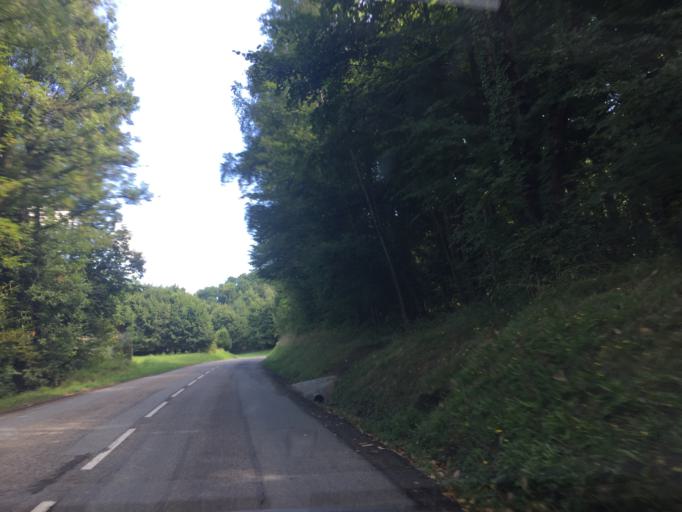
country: FR
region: Rhone-Alpes
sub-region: Departement de la Savoie
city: La Rochette
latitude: 45.4525
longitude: 6.1211
